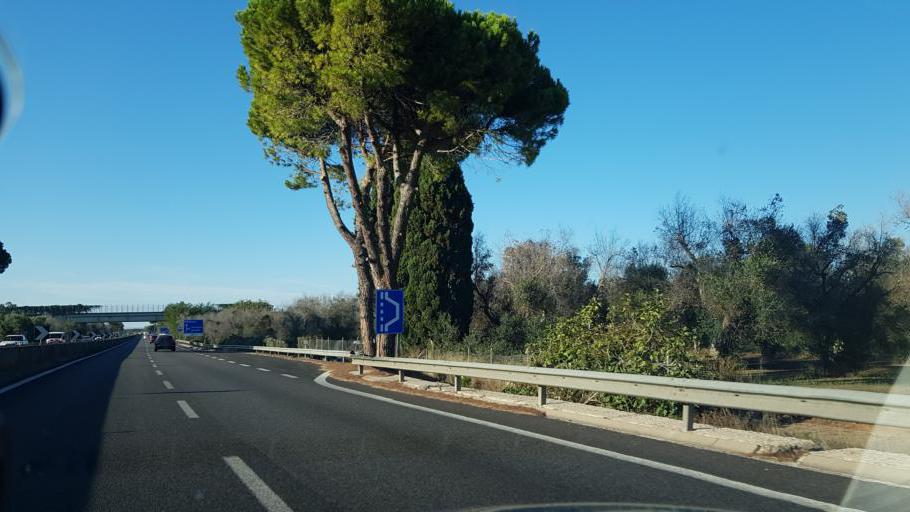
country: IT
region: Apulia
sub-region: Provincia di Lecce
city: Squinzano
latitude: 40.4542
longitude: 18.0646
